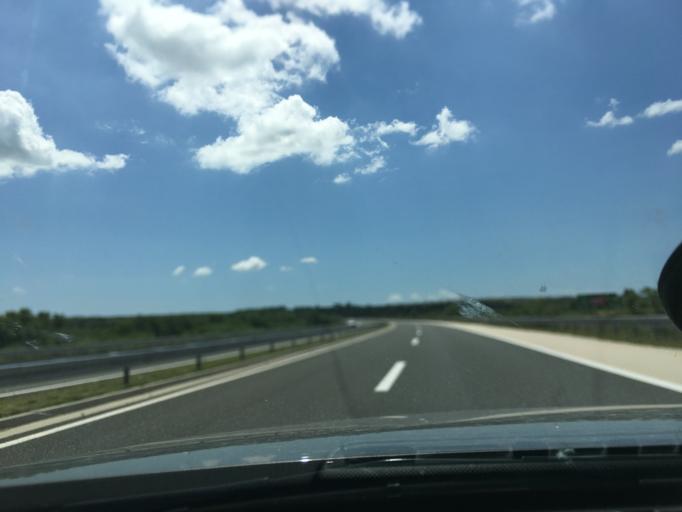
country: HR
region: Zadarska
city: Policnik
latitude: 44.1702
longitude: 15.4223
